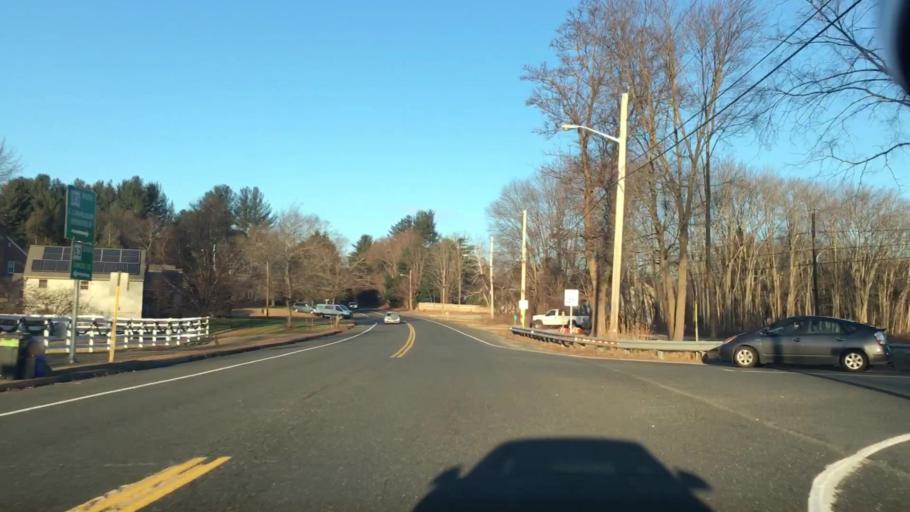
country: US
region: Massachusetts
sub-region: Hampden County
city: East Longmeadow
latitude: 42.0480
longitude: -72.4765
